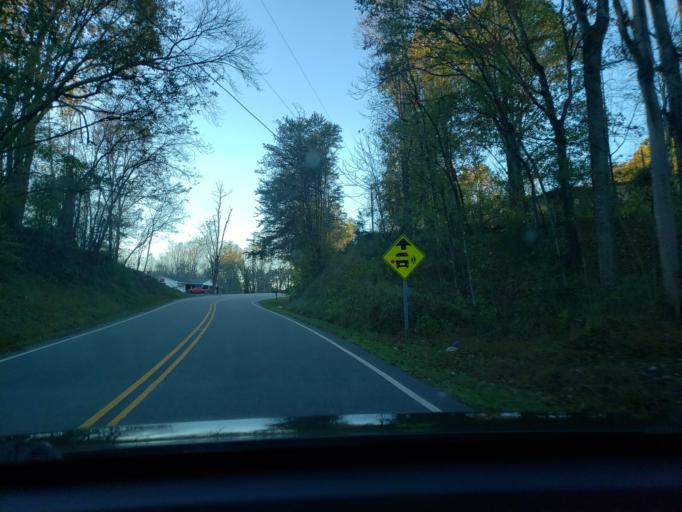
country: US
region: North Carolina
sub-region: Stokes County
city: Danbury
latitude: 36.3961
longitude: -80.1983
